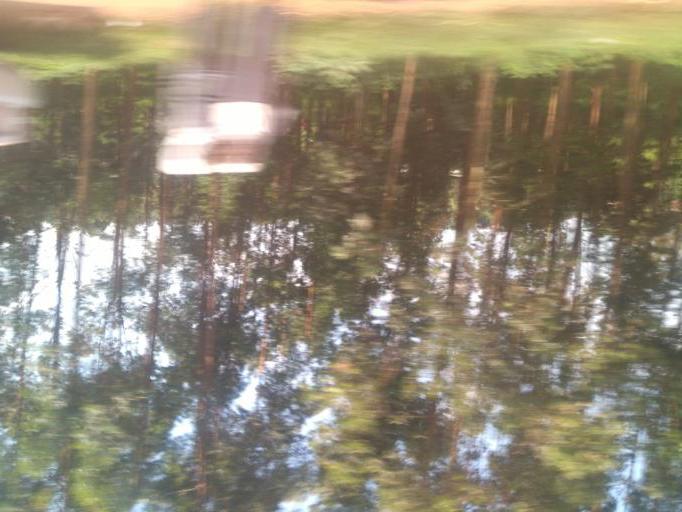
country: UG
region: Central Region
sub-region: Wakiso District
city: Kajansi
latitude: 0.2806
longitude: 32.4831
